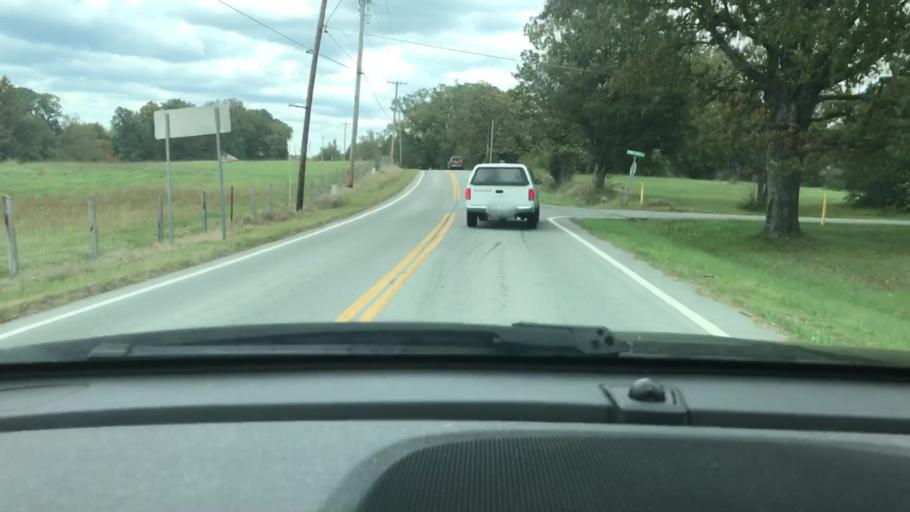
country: US
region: Tennessee
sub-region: Dickson County
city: Charlotte
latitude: 36.2298
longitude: -87.2526
